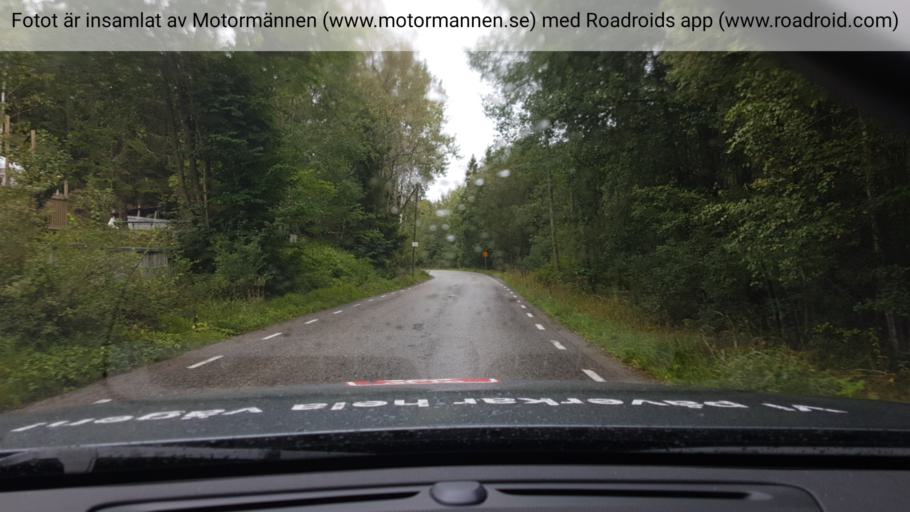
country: SE
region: Stockholm
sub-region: Nynashamns Kommun
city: Osmo
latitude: 59.0492
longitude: 17.8706
